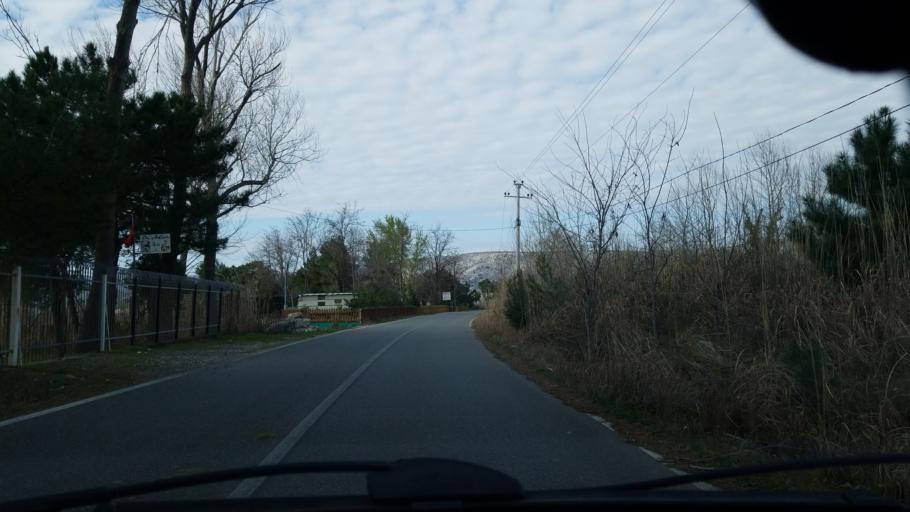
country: AL
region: Lezhe
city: Shengjin
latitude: 41.7831
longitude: 19.6034
